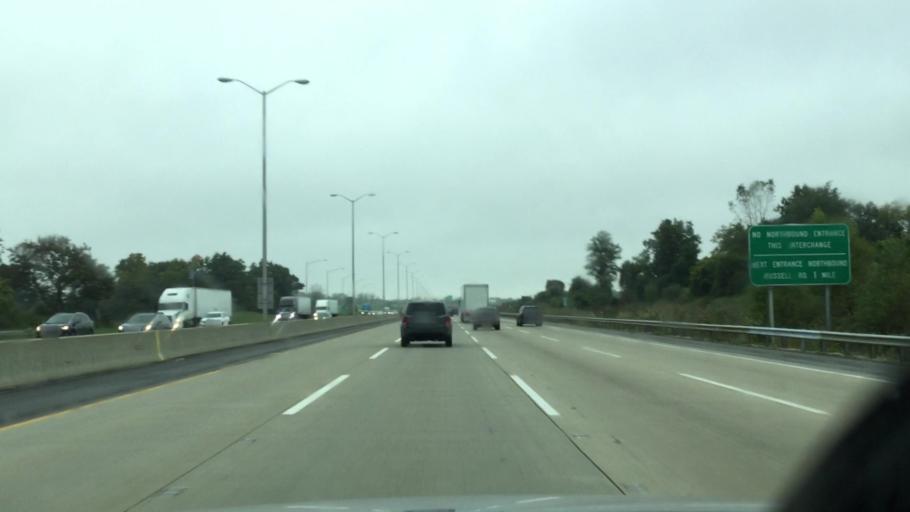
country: US
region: Illinois
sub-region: Lake County
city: Wadsworth
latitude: 42.4568
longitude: -87.9610
